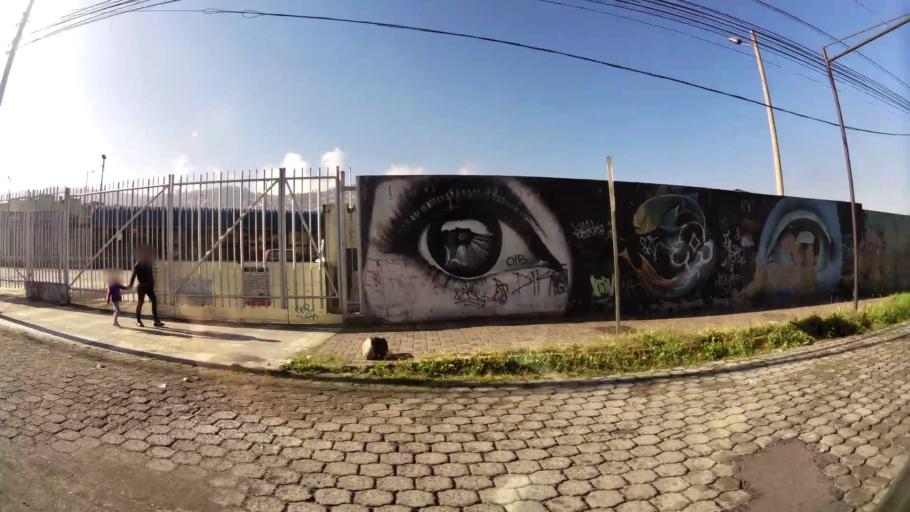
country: EC
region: Pichincha
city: Quito
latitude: -0.2486
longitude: -78.5195
